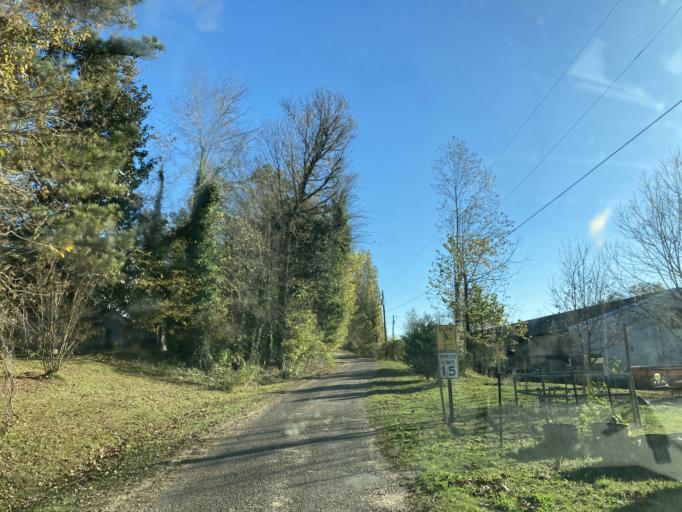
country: US
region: Mississippi
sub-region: Yazoo County
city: Yazoo City
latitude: 32.8165
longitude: -90.4481
